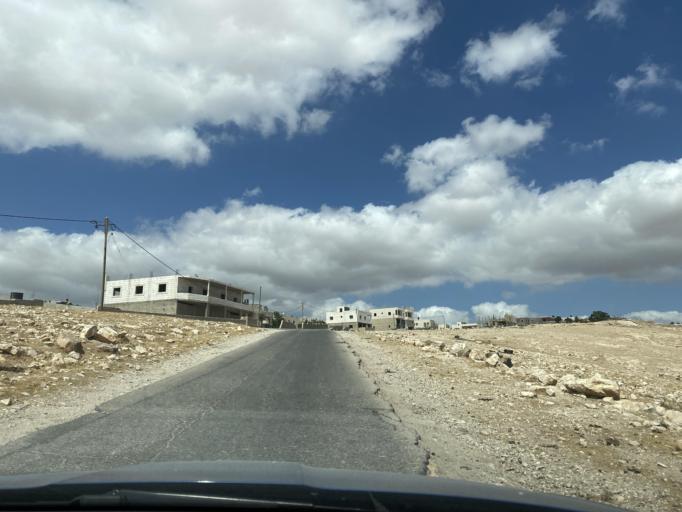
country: PS
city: `Arab ar Rashaydah
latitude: 31.5702
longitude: 35.2347
